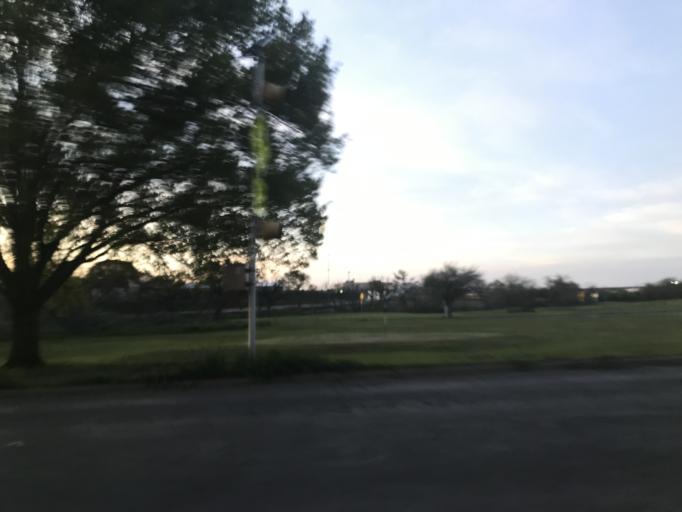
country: US
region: Texas
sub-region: Tom Green County
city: San Angelo
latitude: 31.4605
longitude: -100.4479
